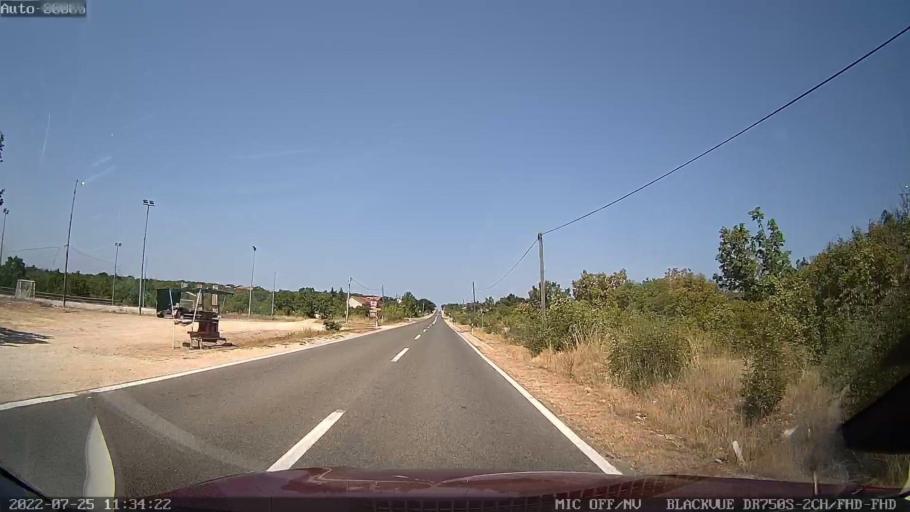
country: HR
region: Zadarska
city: Posedarje
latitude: 44.2297
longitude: 15.4225
